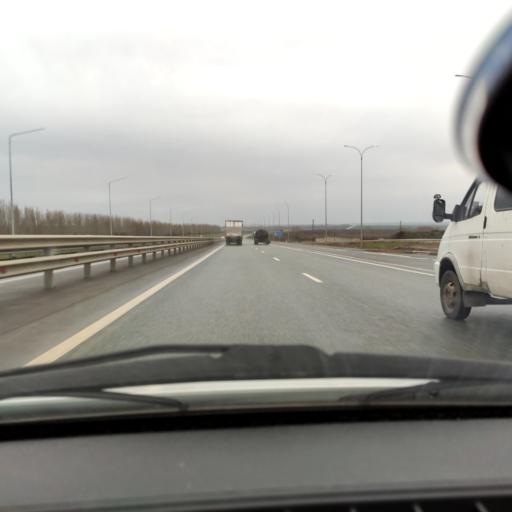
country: RU
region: Bashkortostan
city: Tolbazy
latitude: 54.2007
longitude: 55.8871
